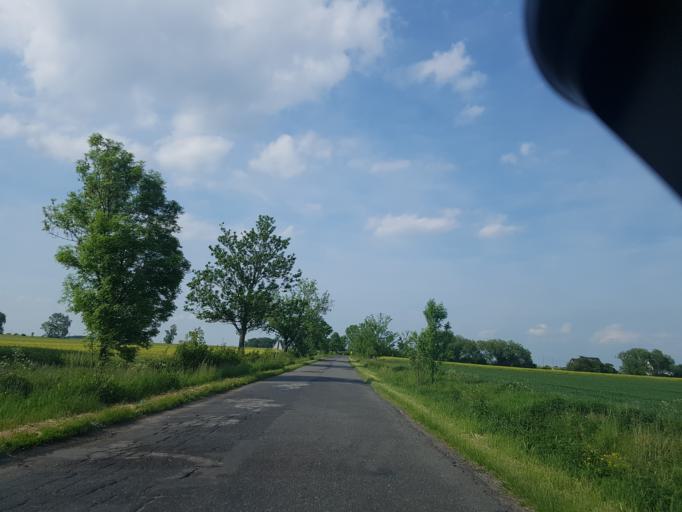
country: PL
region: Lower Silesian Voivodeship
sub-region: Powiat olawski
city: Wierzbno
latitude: 50.9080
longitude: 17.1103
